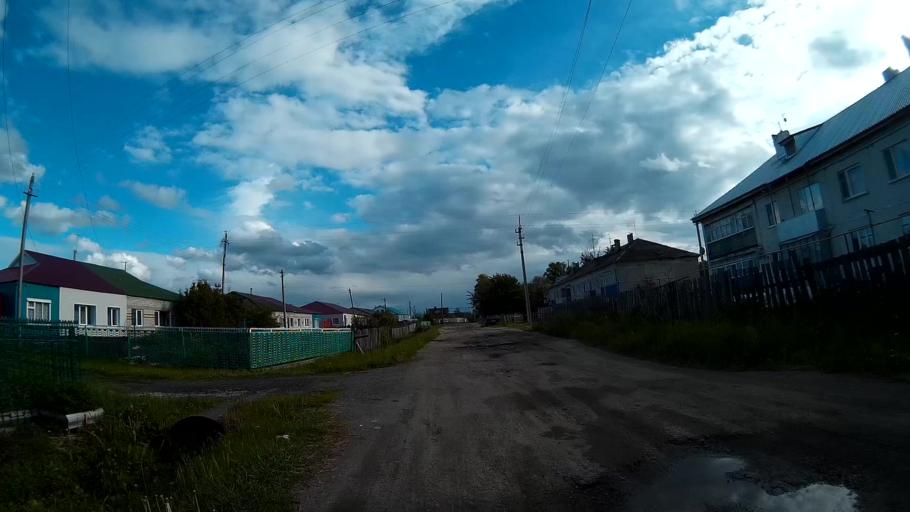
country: RU
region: Ulyanovsk
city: Novoul'yanovsk
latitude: 54.2027
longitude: 48.2688
